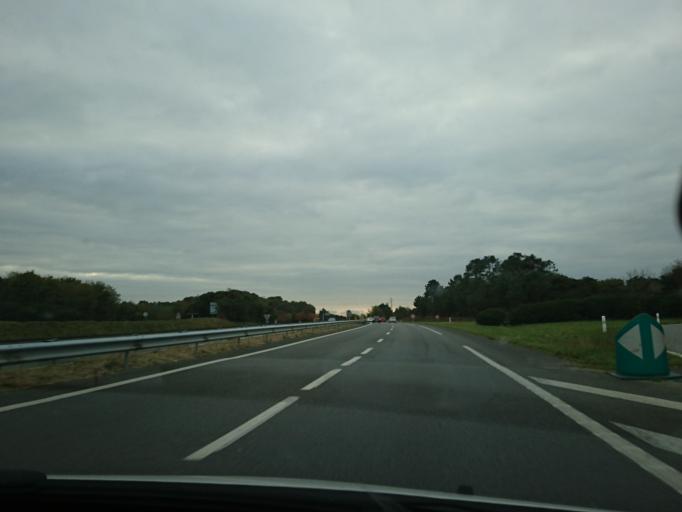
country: FR
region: Brittany
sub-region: Departement du Morbihan
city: Marzan
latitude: 47.5309
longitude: -2.3058
